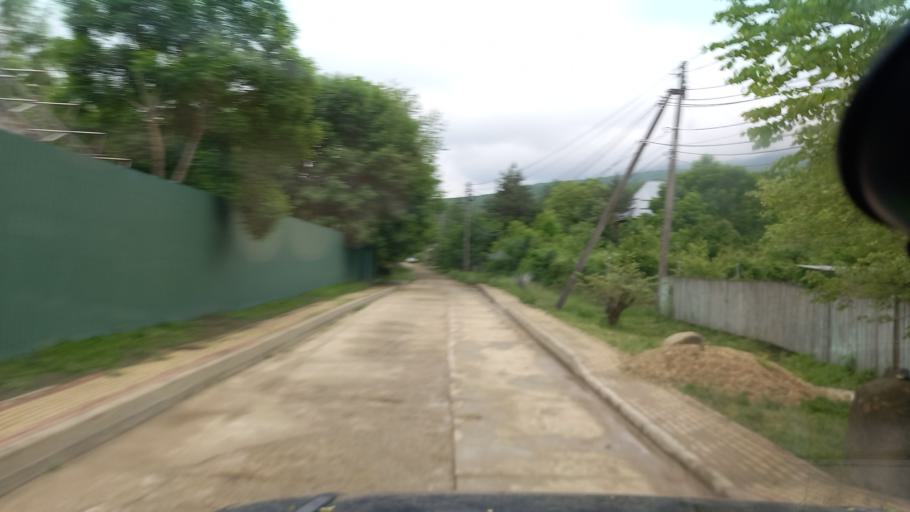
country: RU
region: Krasnodarskiy
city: Azovskaya
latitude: 44.6377
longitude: 38.6176
